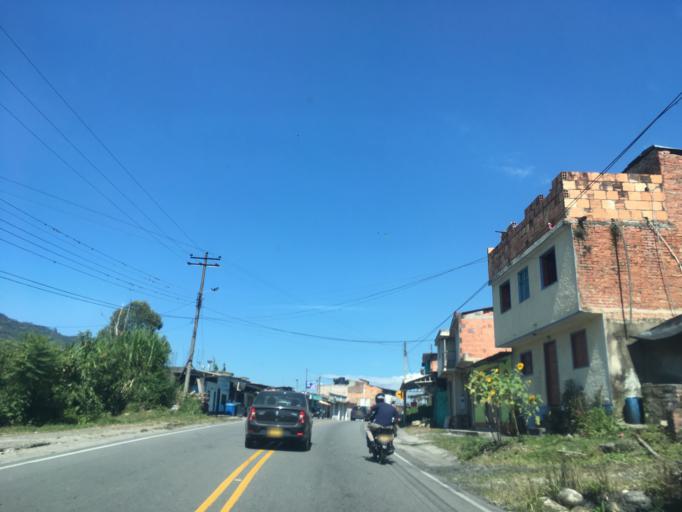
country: CO
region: Santander
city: Suaita
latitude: 6.0679
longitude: -73.4150
